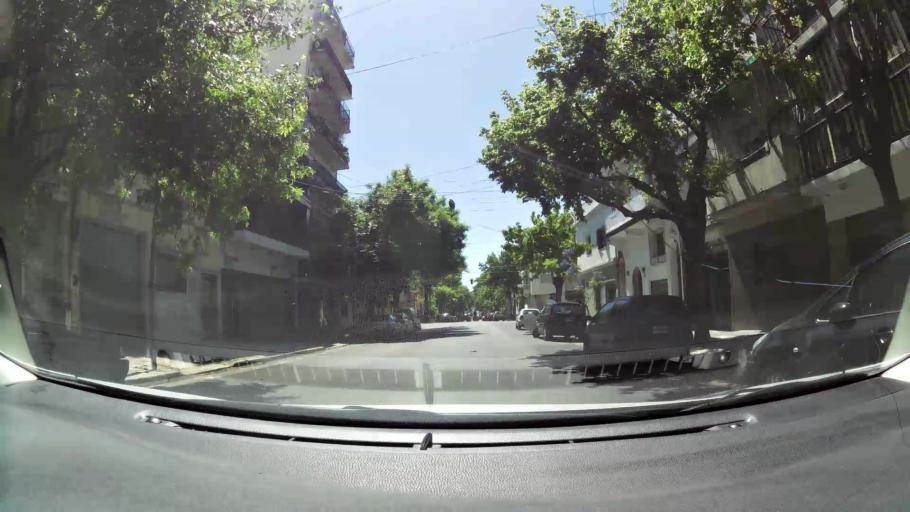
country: AR
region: Buenos Aires F.D.
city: Buenos Aires
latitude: -34.6299
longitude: -58.4150
